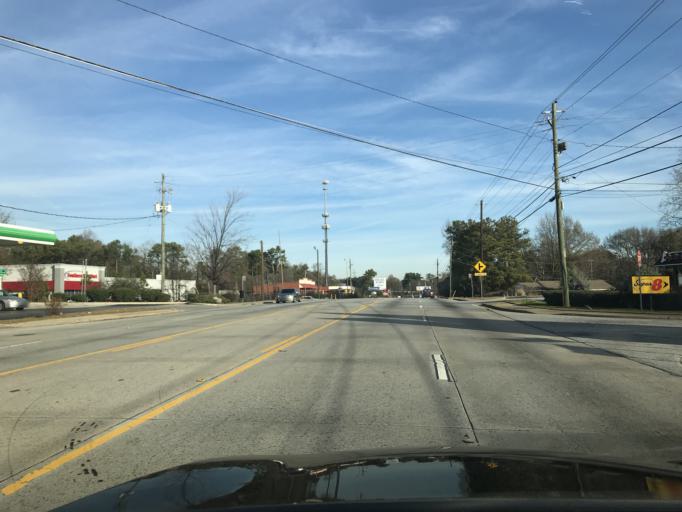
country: US
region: Georgia
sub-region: Clayton County
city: Forest Park
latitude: 33.5873
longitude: -84.3781
